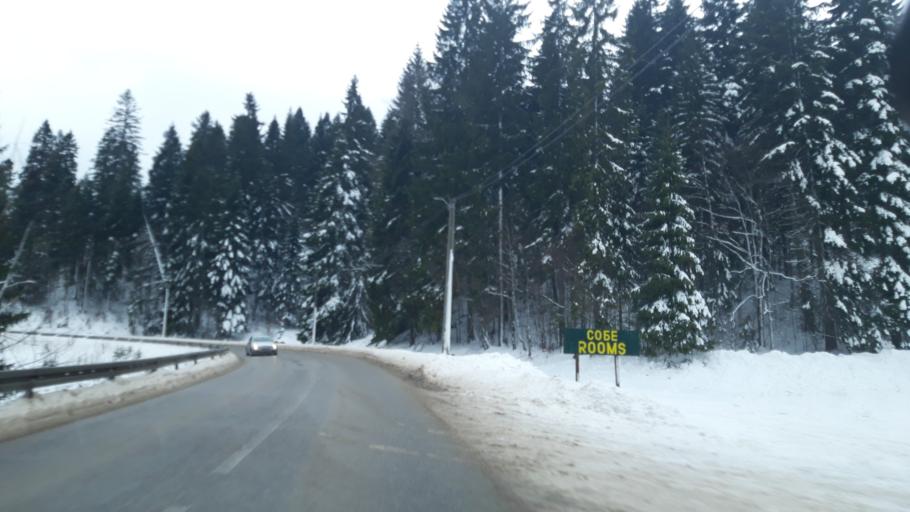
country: BA
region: Republika Srpska
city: Han Pijesak
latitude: 44.0882
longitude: 18.9529
